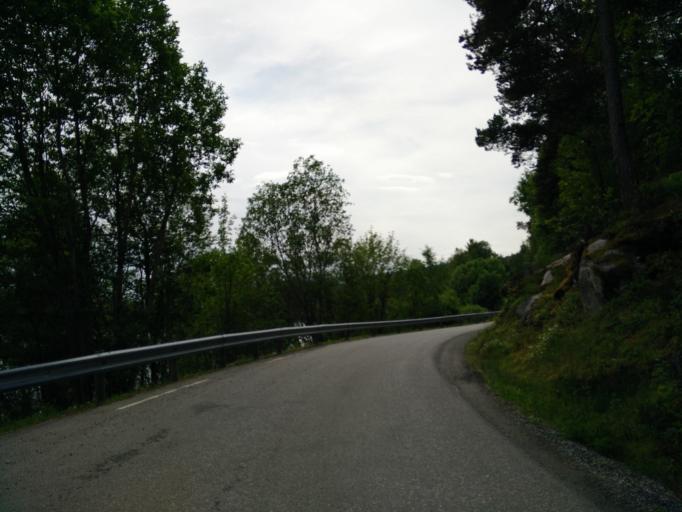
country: NO
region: More og Romsdal
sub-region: Kristiansund
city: Rensvik
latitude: 63.0257
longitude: 7.9530
